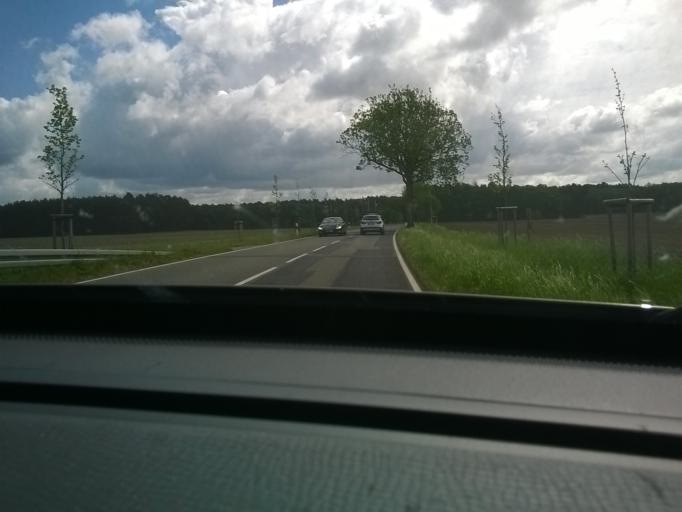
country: DE
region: Brandenburg
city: Wittstock
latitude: 53.0754
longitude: 12.5042
